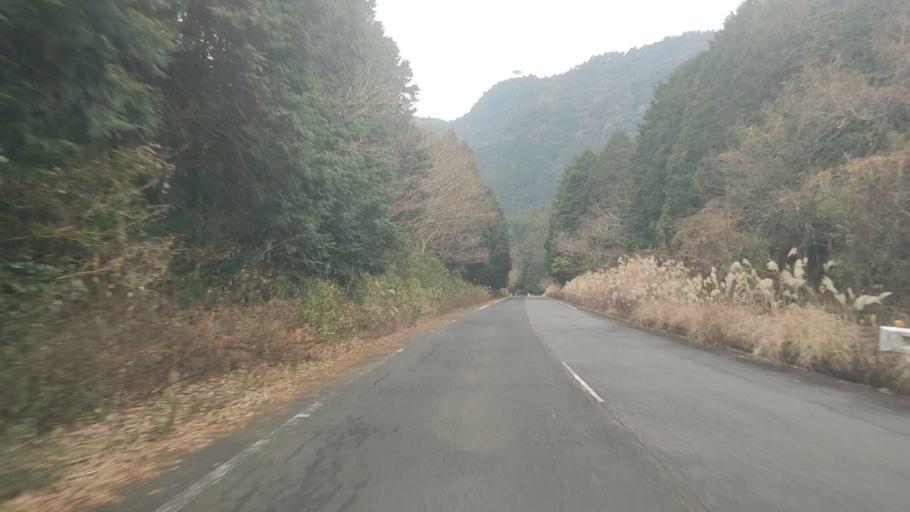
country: JP
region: Nagasaki
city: Shimabara
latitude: 32.7949
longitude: 130.2848
